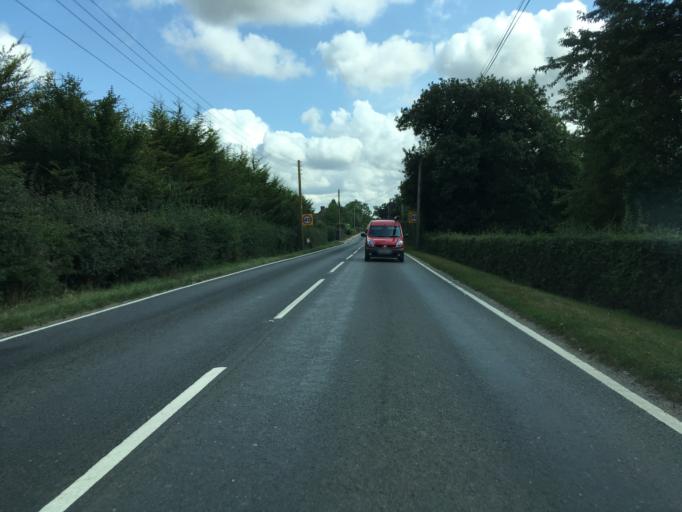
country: GB
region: England
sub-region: Kent
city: Headcorn
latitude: 51.1795
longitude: 0.6121
